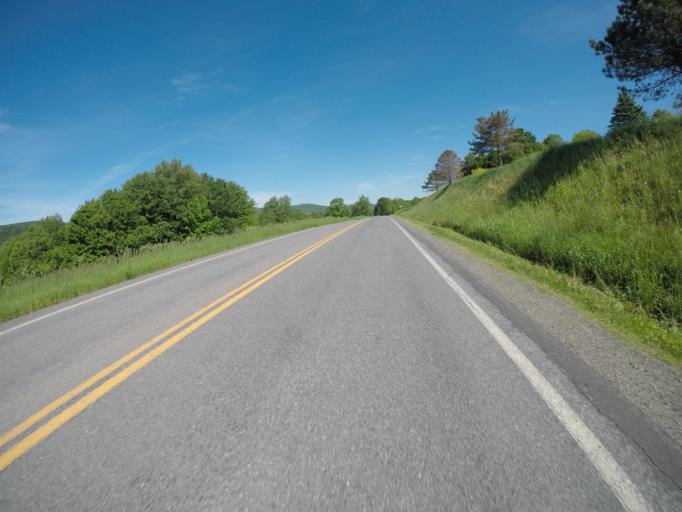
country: US
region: New York
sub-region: Delaware County
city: Delhi
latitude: 42.1843
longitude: -74.8003
